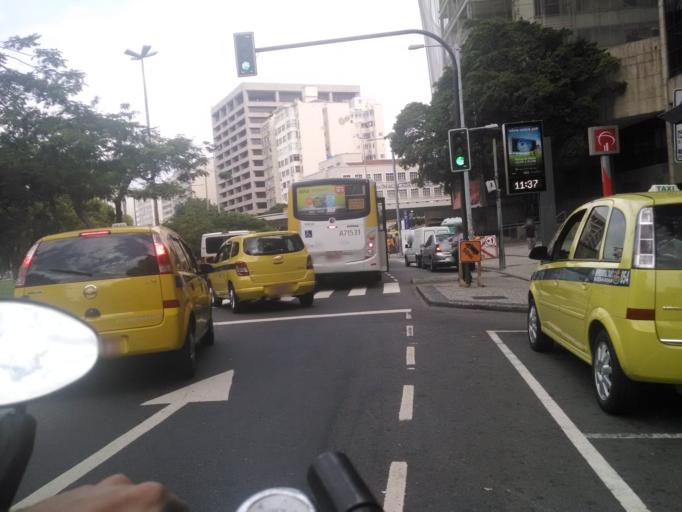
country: BR
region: Rio de Janeiro
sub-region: Rio De Janeiro
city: Rio de Janeiro
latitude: -22.9424
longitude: -43.1809
